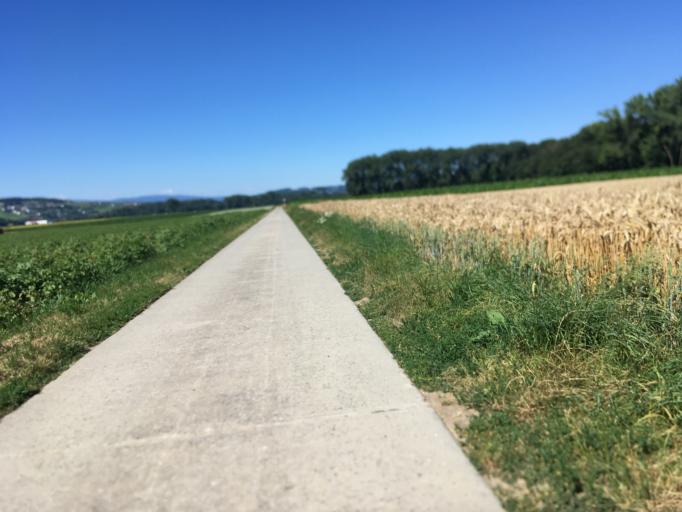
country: CH
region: Vaud
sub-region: Broye-Vully District
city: Avenches
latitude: 46.8949
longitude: 7.0233
